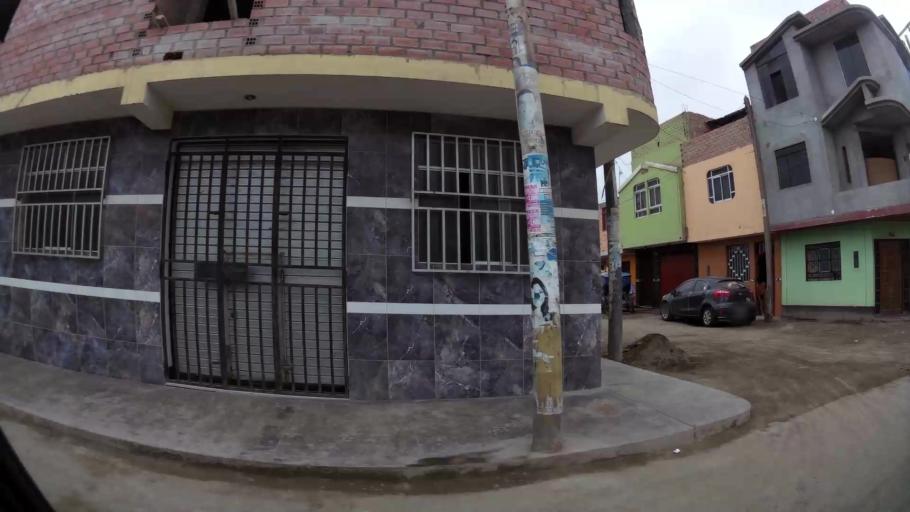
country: PE
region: Lima
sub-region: Barranca
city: Paramonga
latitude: -10.6740
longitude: -77.8147
